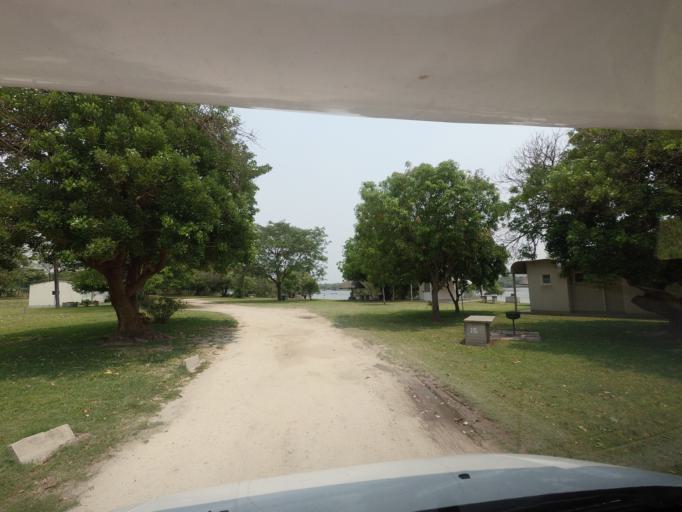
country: ZM
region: Western
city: Sesheke
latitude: -17.4864
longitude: 24.2851
